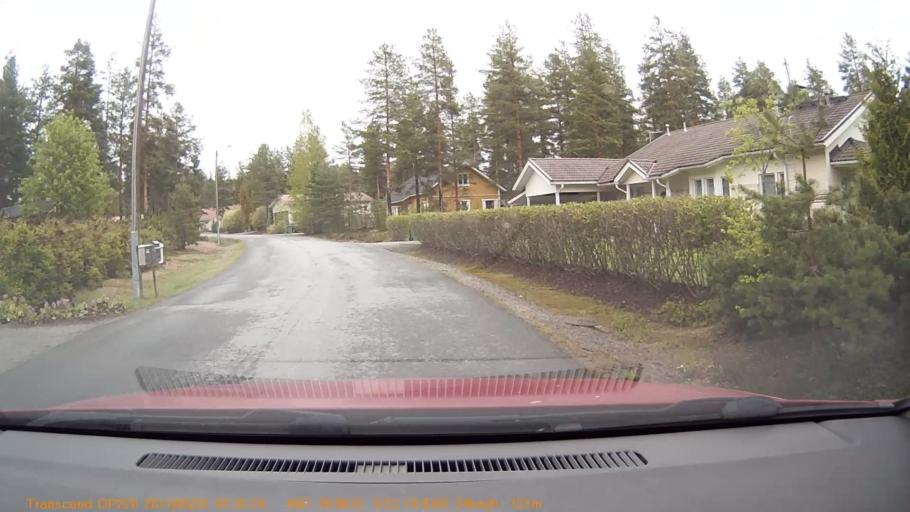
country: FI
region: Pirkanmaa
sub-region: Tampere
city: Haemeenkyroe
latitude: 61.6644
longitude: 23.2339
